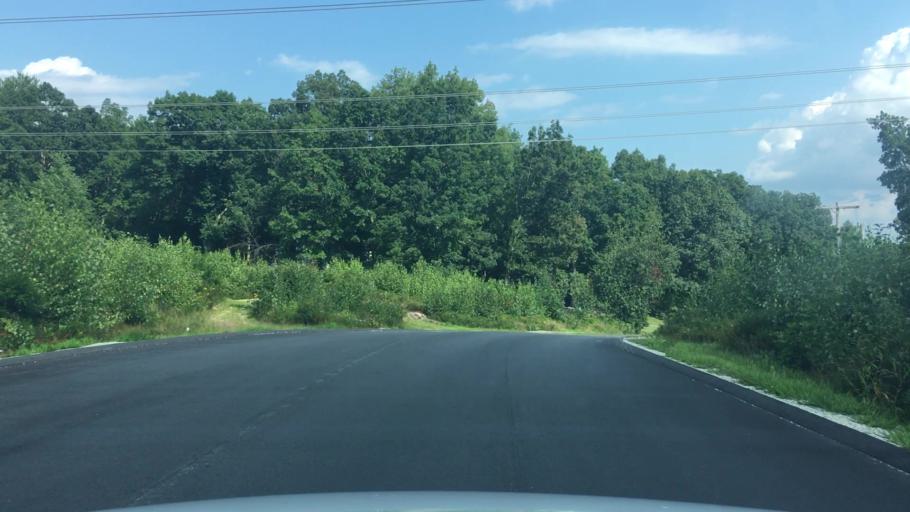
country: US
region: New Hampshire
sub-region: Rockingham County
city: Derry Village
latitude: 42.9292
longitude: -71.3178
